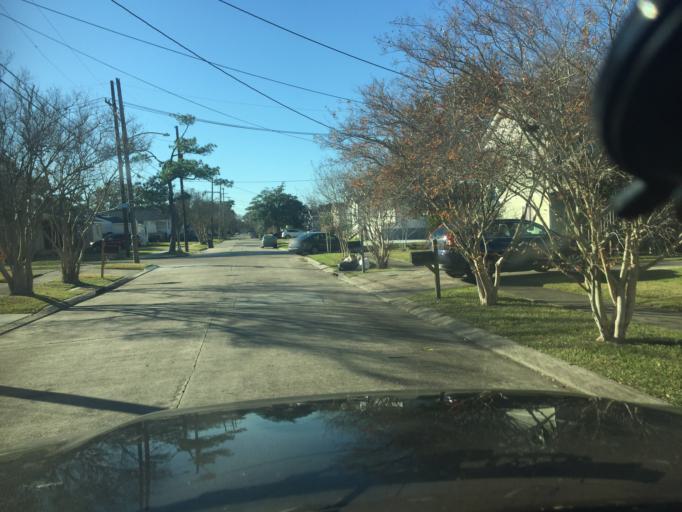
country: US
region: Louisiana
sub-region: Orleans Parish
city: New Orleans
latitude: 29.9899
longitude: -90.0820
